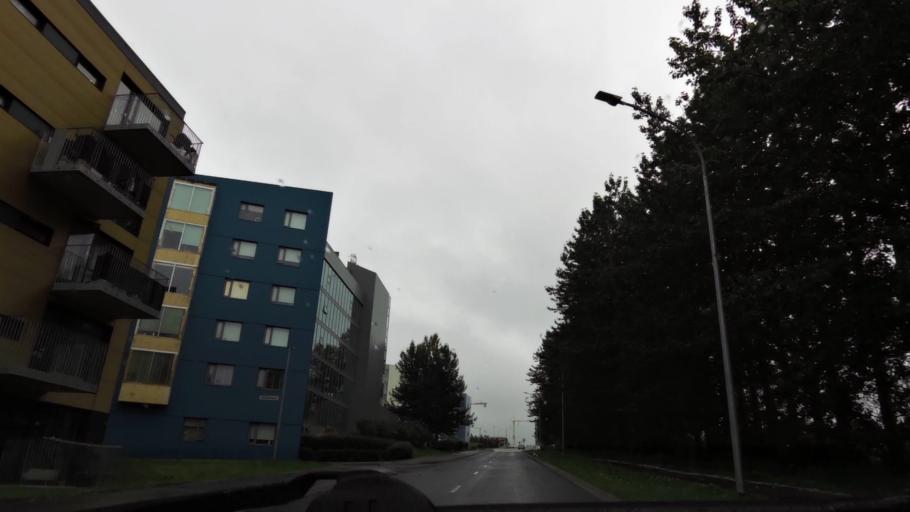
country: IS
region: Capital Region
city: Reykjavik
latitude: 64.1218
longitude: -21.8931
